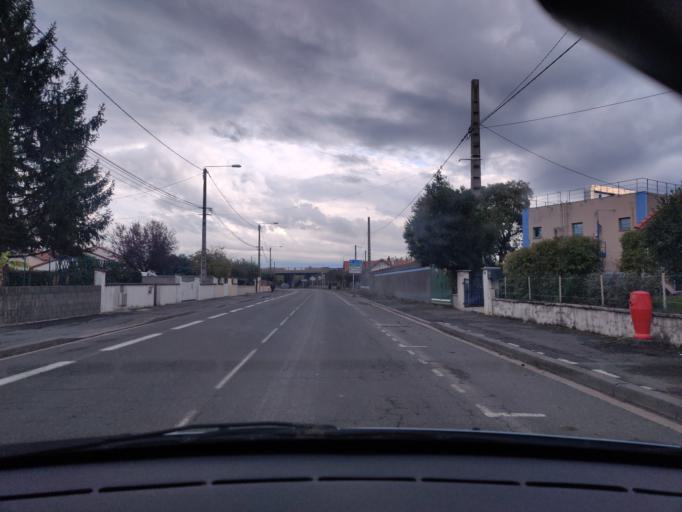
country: FR
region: Auvergne
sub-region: Departement du Puy-de-Dome
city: Menetrol
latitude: 45.8813
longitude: 3.1274
